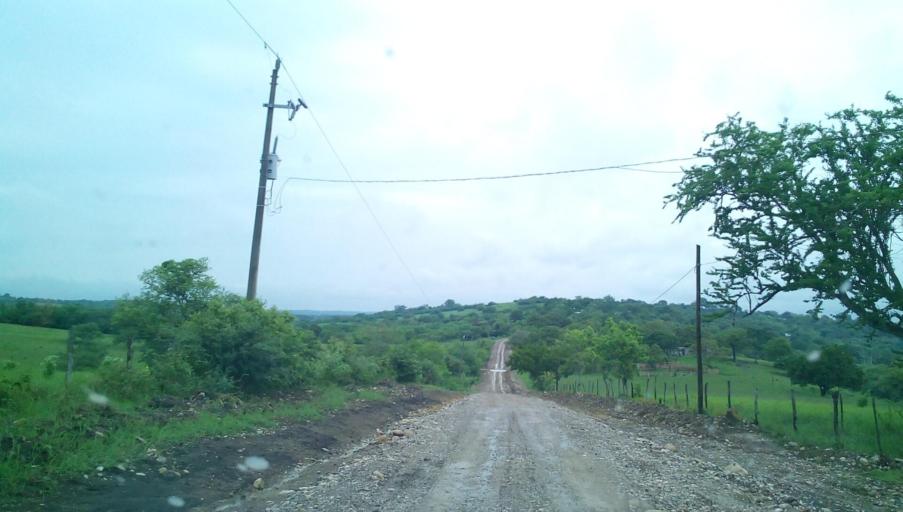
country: MX
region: Veracruz
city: Tempoal de Sanchez
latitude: 21.4551
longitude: -98.4274
